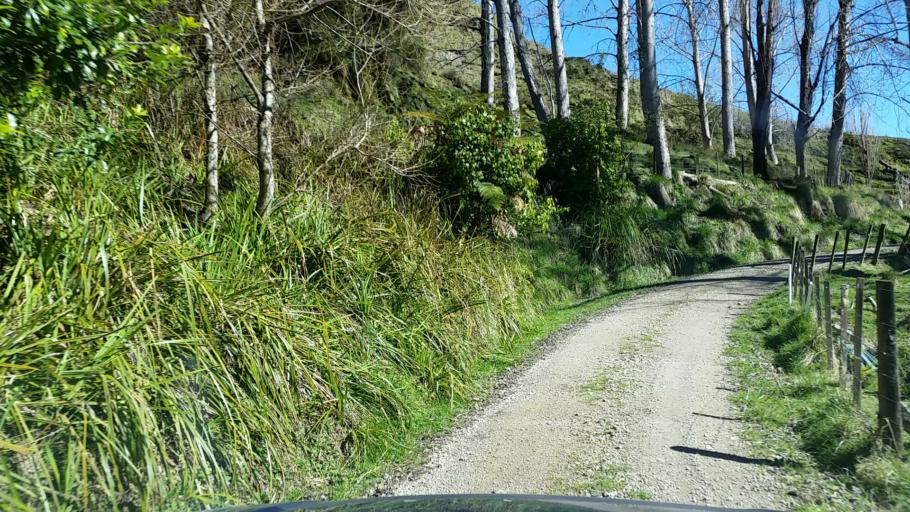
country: NZ
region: Taranaki
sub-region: South Taranaki District
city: Patea
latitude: -39.6209
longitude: 174.8258
